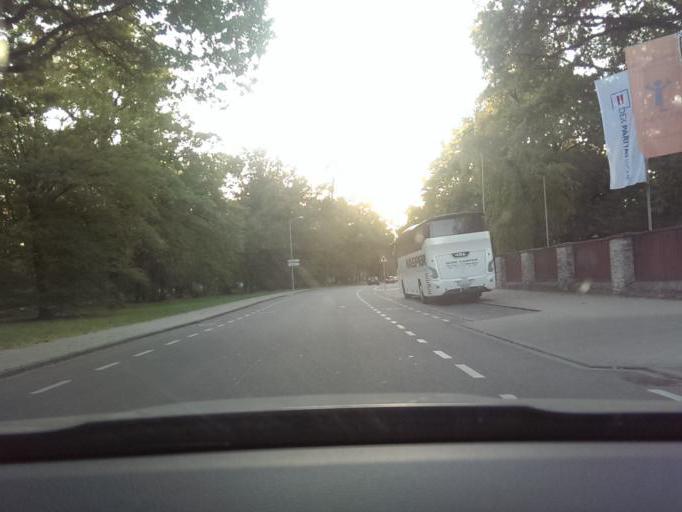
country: DE
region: Baden-Wuerttemberg
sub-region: Karlsruhe Region
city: Karlsruhe
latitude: 49.0299
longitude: 8.3939
